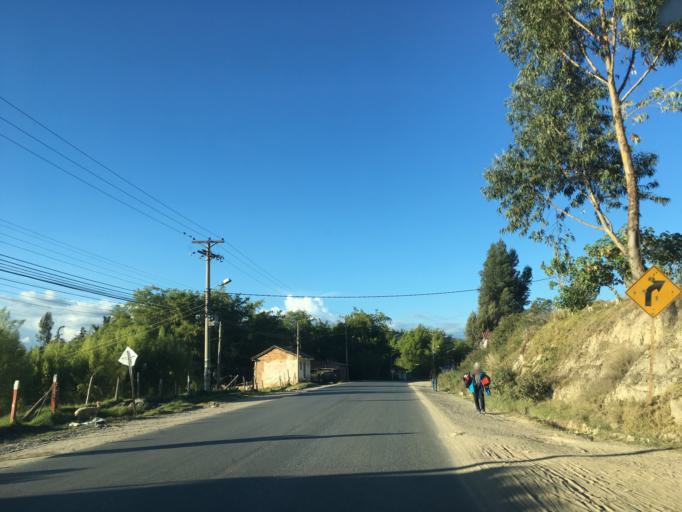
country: CO
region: Boyaca
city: Sogamoso
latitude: 5.6975
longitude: -72.9404
